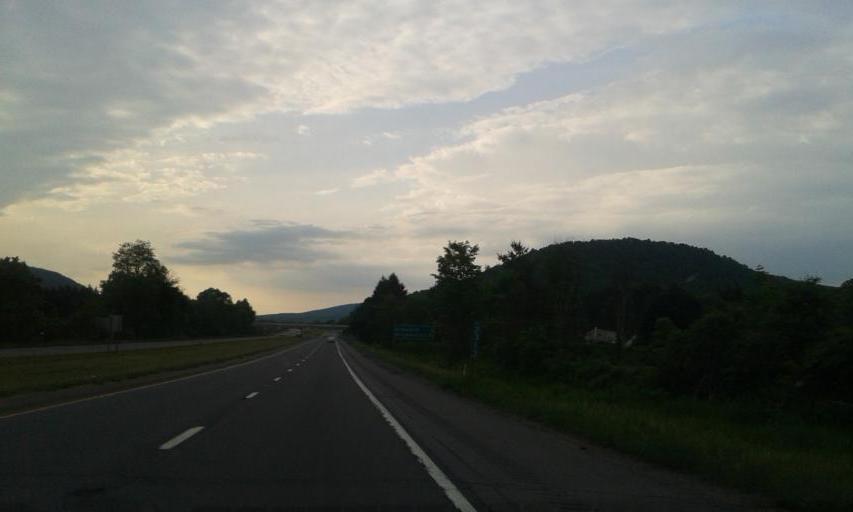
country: US
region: Pennsylvania
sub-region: Susquehanna County
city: Hallstead
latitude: 41.9776
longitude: -75.7426
